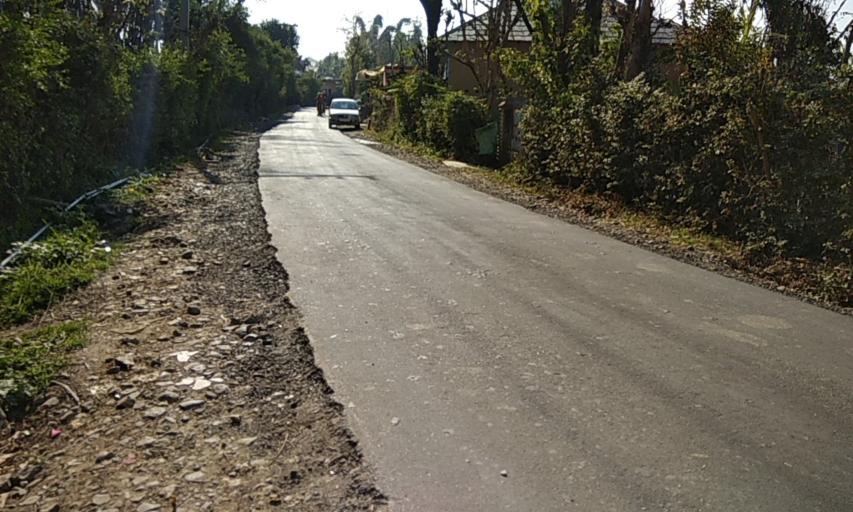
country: IN
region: Himachal Pradesh
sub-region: Kangra
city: Palampur
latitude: 32.1157
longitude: 76.5253
